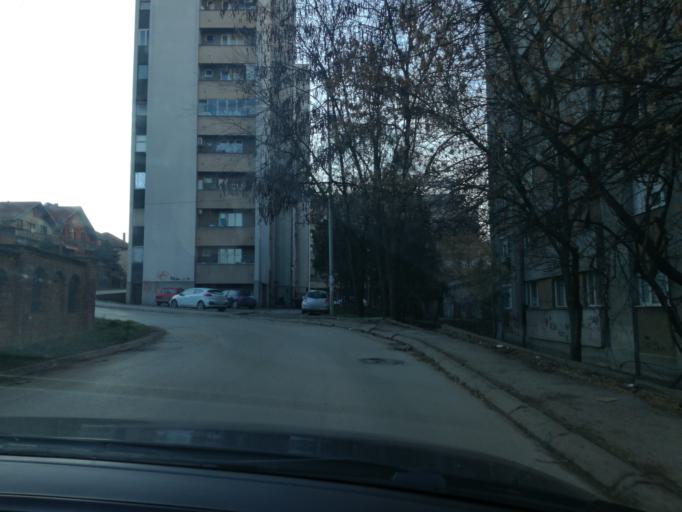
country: RS
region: Central Serbia
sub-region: Nisavski Okrug
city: Nis
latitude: 43.3111
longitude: 21.8877
